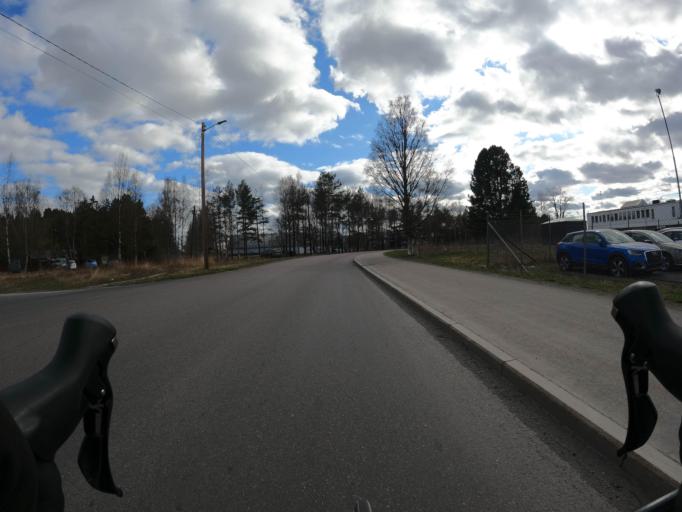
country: NO
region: Akershus
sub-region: Skedsmo
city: Lillestrom
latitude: 59.9643
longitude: 11.0708
